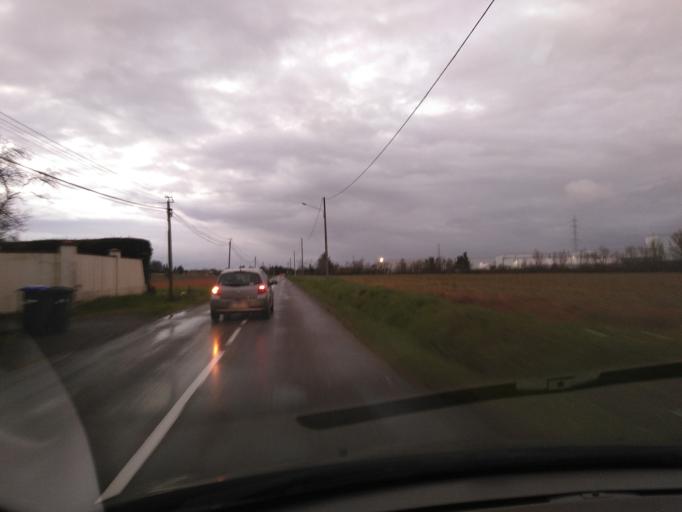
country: FR
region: Midi-Pyrenees
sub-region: Departement de la Haute-Garonne
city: Seilh
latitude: 43.6784
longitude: 1.3469
